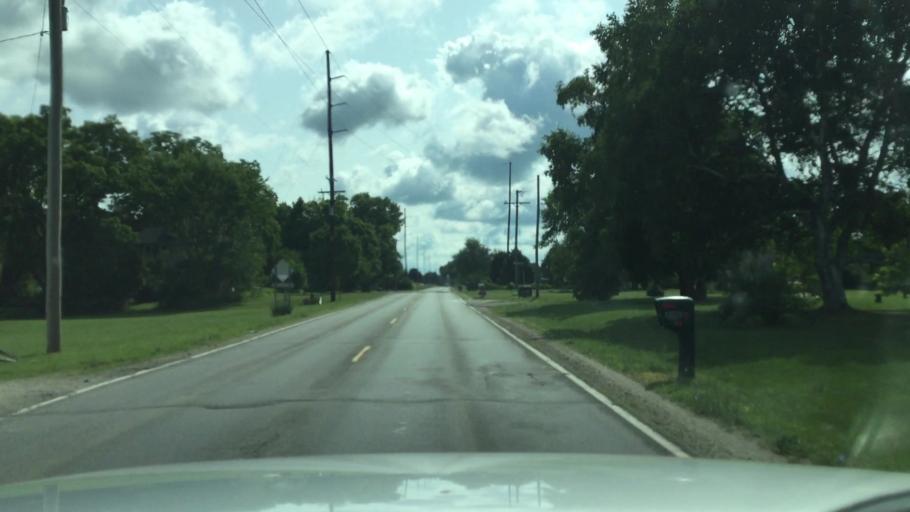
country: US
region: Michigan
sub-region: Montcalm County
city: Greenville
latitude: 43.1924
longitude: -85.2201
